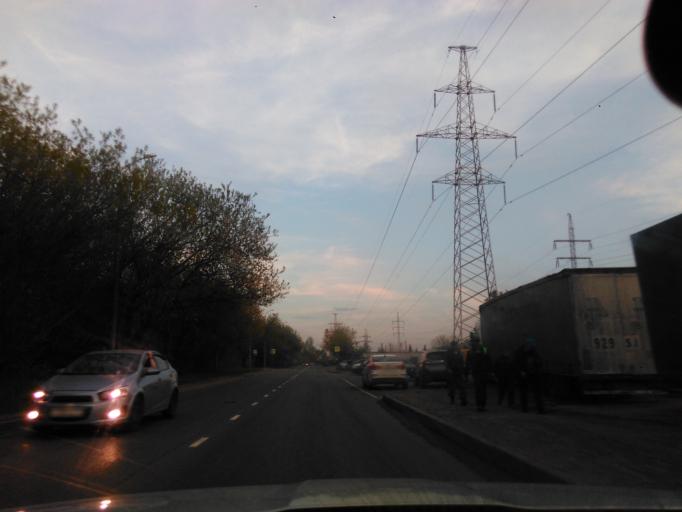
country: RU
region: Moscow
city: Kapotnya
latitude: 55.6632
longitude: 37.8094
